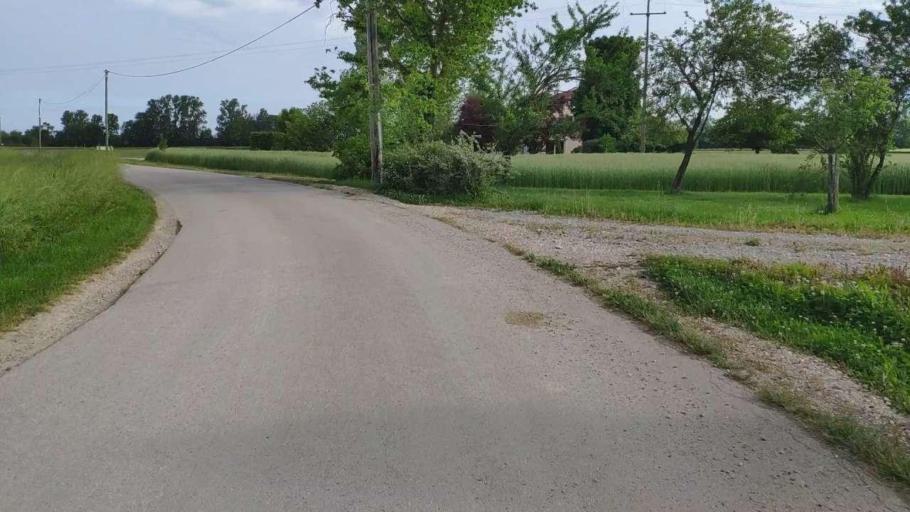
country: FR
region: Franche-Comte
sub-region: Departement du Jura
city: Bletterans
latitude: 46.7348
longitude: 5.4743
